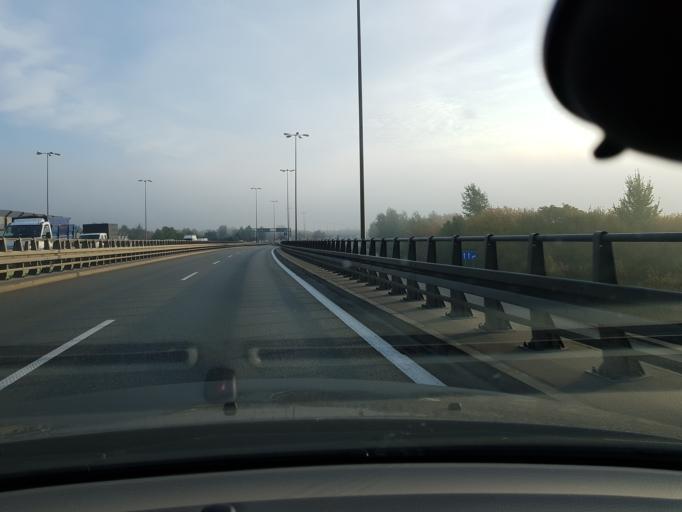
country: PL
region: Masovian Voivodeship
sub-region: Warszawa
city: Mokotow
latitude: 52.1991
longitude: 21.0539
